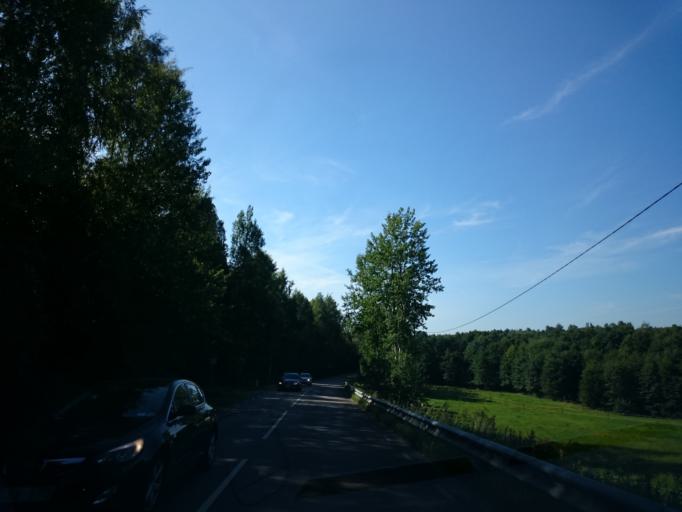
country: SE
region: OEstergoetland
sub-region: Norrkopings Kommun
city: Krokek
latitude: 58.6673
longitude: 16.4100
